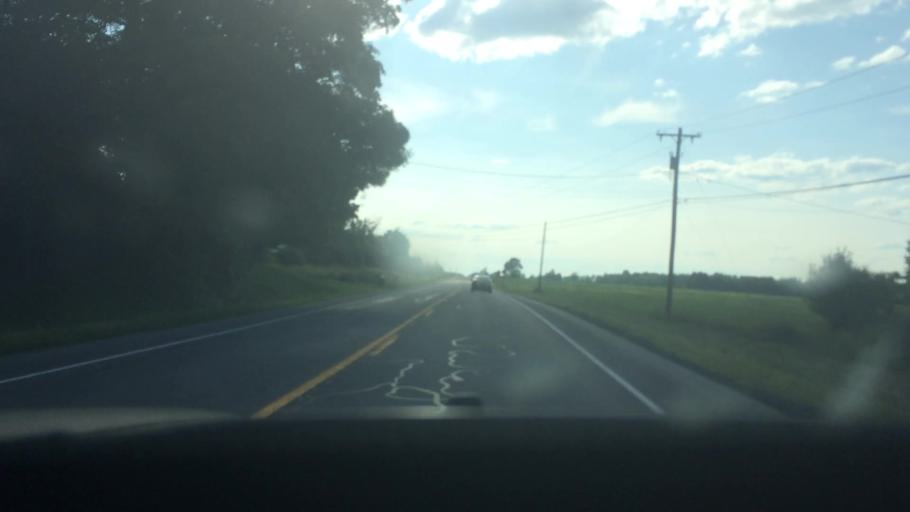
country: US
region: New York
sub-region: St. Lawrence County
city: Potsdam
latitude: 44.6897
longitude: -74.7465
